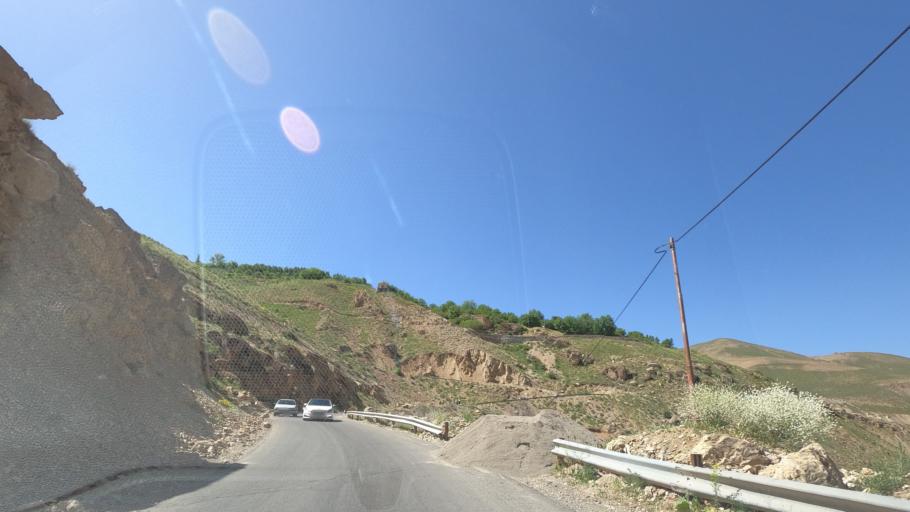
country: IR
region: Alborz
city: Karaj
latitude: 35.9249
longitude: 51.1565
